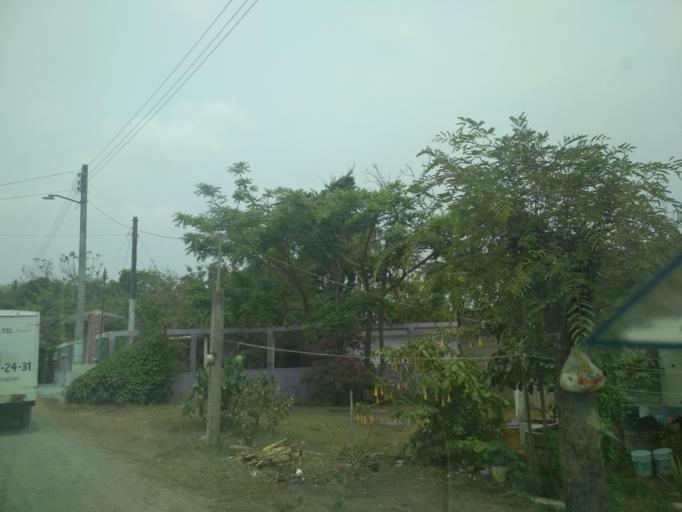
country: MX
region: Veracruz
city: El Tejar
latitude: 19.0487
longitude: -96.1683
